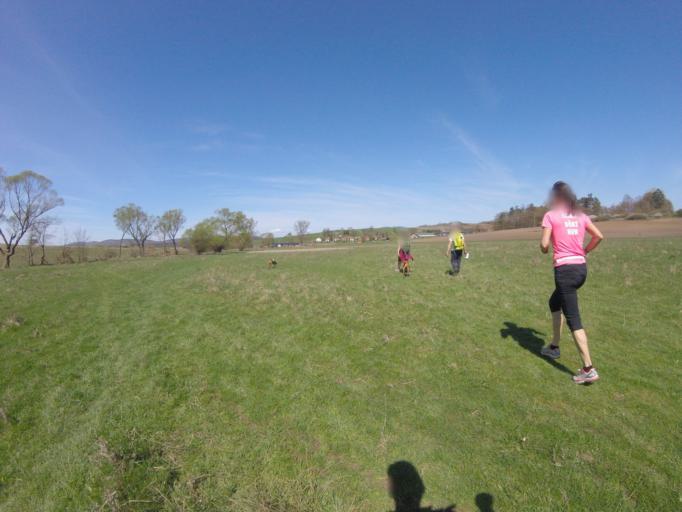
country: HU
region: Borsod-Abauj-Zemplen
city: Szendro
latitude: 48.4135
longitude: 20.7761
